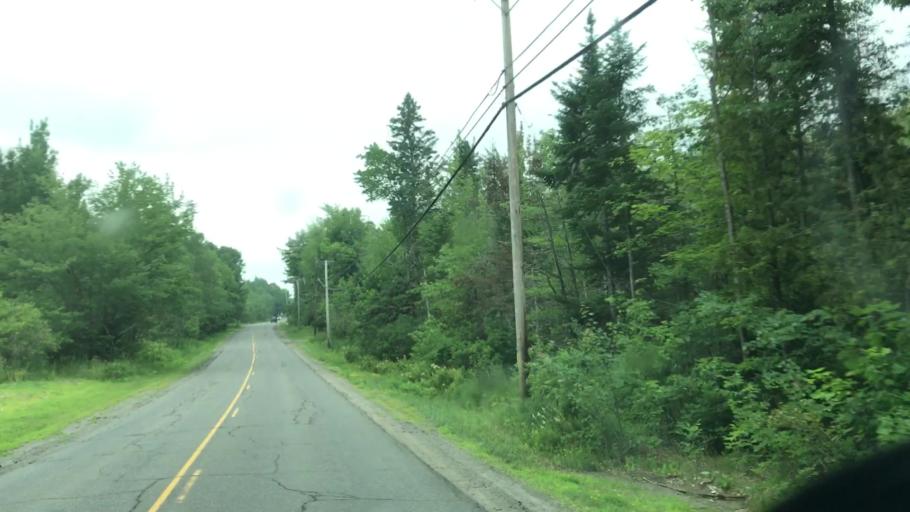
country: US
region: Maine
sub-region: Penobscot County
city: Orono
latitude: 44.8844
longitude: -68.7086
